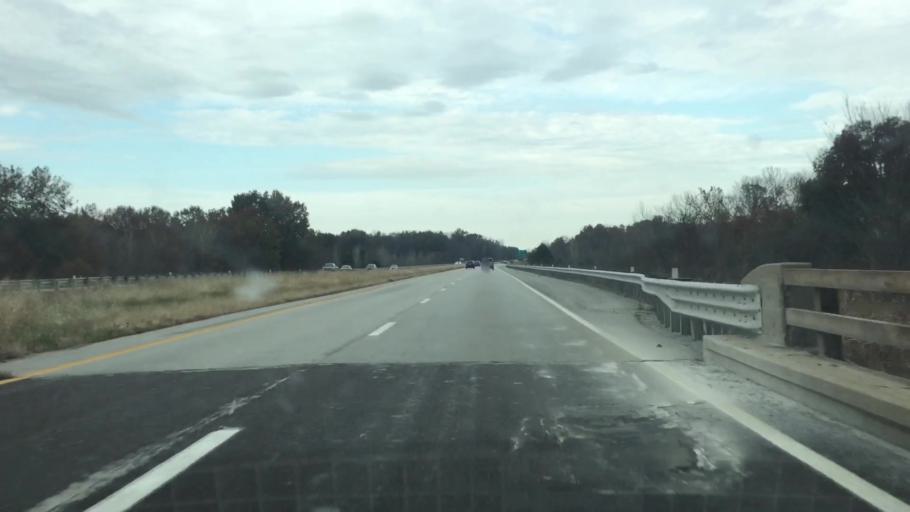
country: US
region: Missouri
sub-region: Henry County
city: Clinton
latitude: 38.2273
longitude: -93.7621
